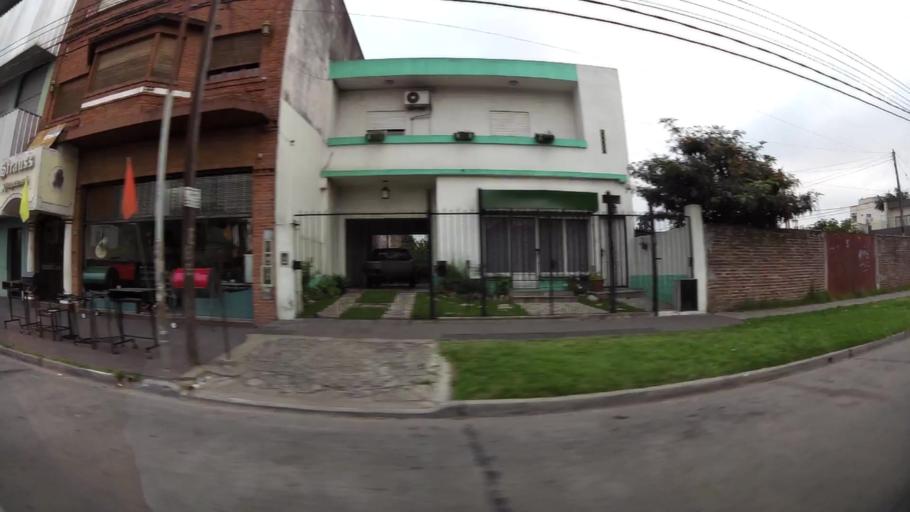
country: AR
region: Buenos Aires
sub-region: Partido de Moron
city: Moron
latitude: -34.6572
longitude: -58.5905
